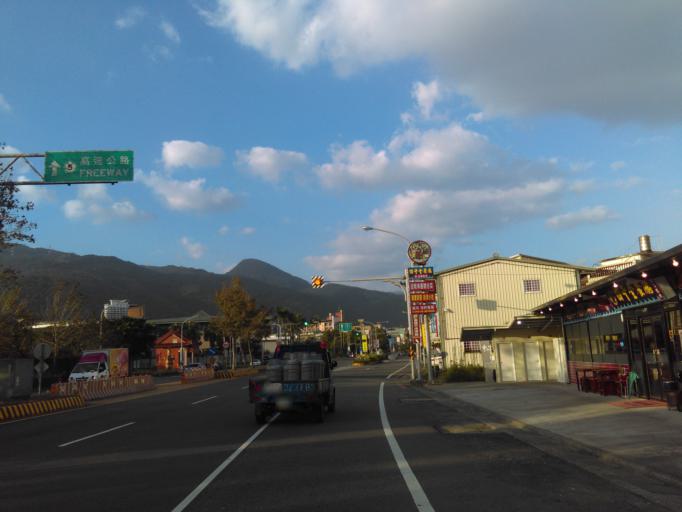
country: TW
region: Taiwan
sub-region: Yilan
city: Yilan
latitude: 24.8149
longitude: 121.7677
